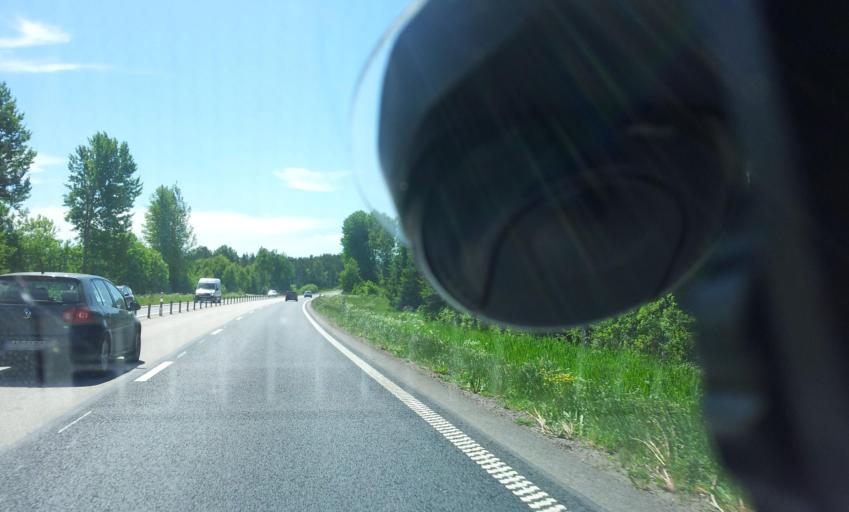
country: SE
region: Kalmar
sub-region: Oskarshamns Kommun
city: Oskarshamn
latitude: 57.3616
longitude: 16.4945
